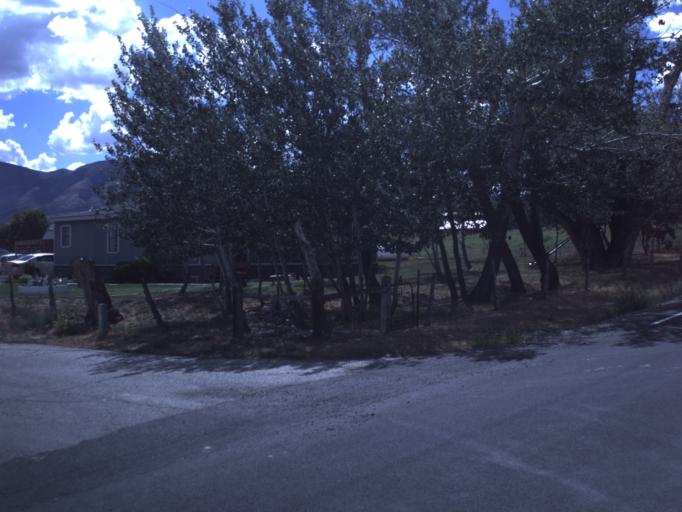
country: US
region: Utah
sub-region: Tooele County
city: Grantsville
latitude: 40.3382
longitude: -112.4792
